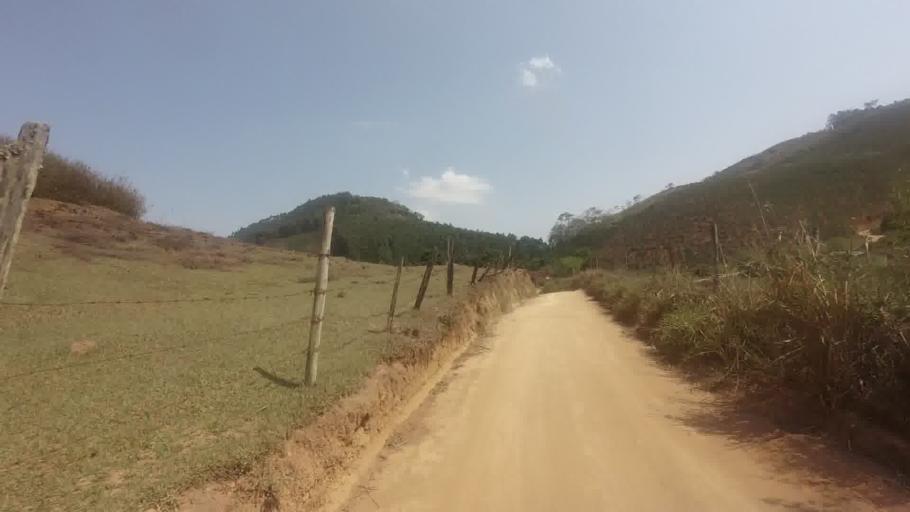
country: BR
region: Espirito Santo
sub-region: Mimoso Do Sul
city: Mimoso do Sul
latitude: -20.9964
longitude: -41.5024
